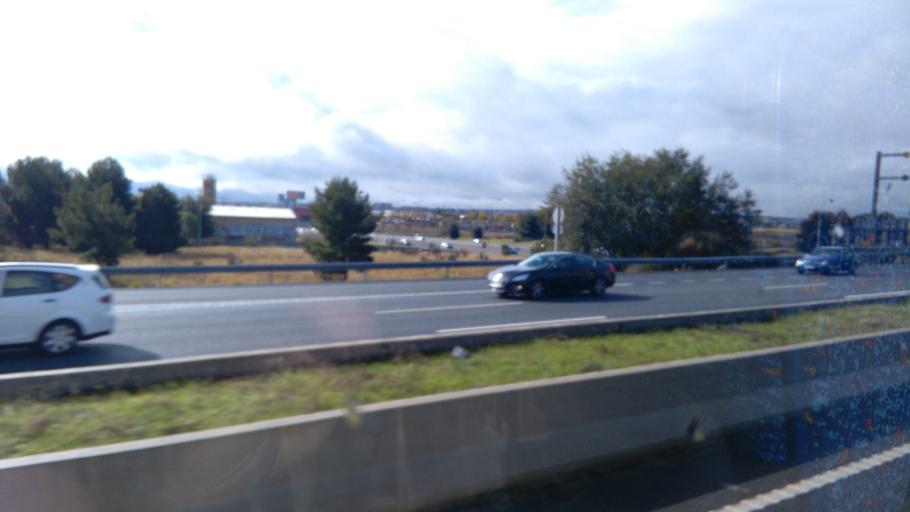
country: ES
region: Madrid
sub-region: Provincia de Madrid
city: Villaverde
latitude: 40.3649
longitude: -3.7193
